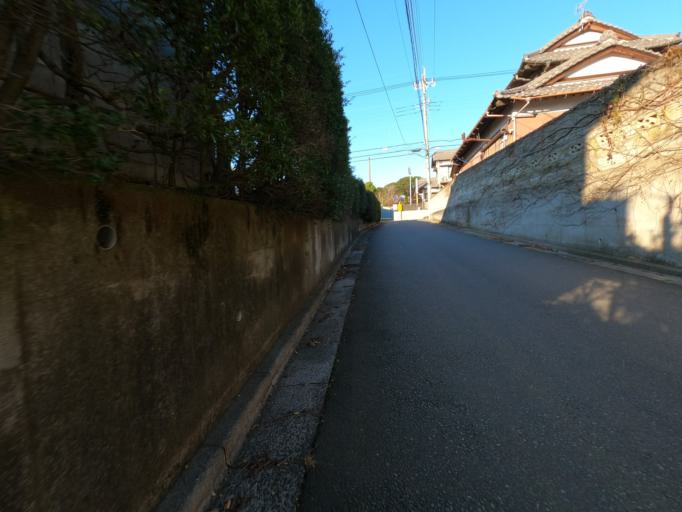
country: JP
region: Ibaraki
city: Moriya
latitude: 35.9361
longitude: 140.0026
